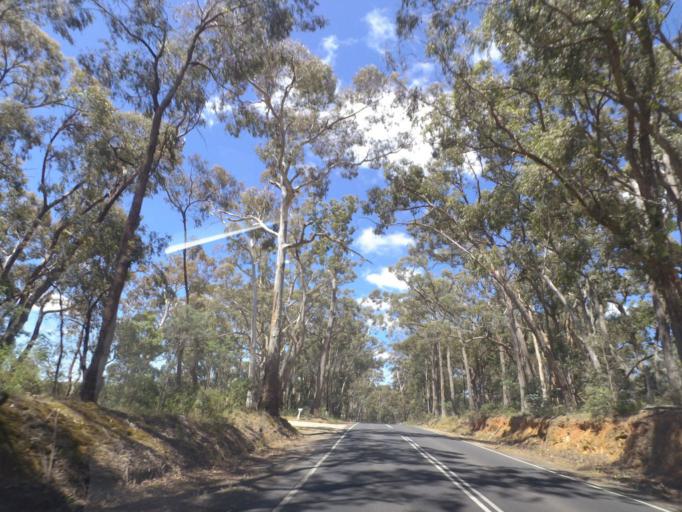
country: AU
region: Victoria
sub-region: Mount Alexander
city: Castlemaine
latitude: -37.2876
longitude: 144.2759
